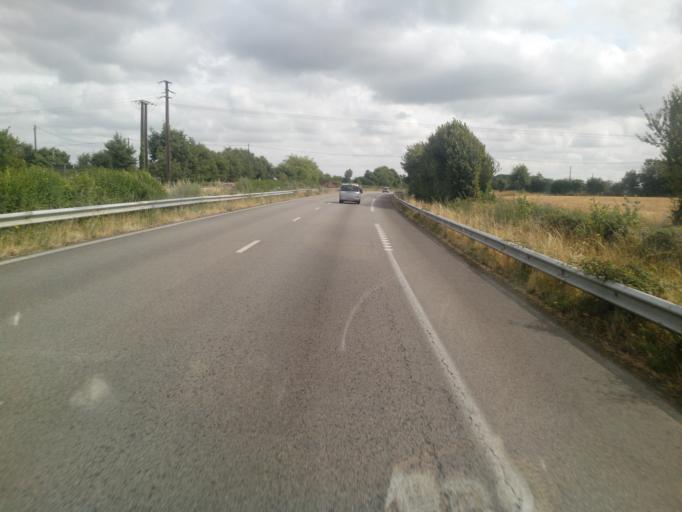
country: FR
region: Pays de la Loire
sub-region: Departement de la Loire-Atlantique
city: Nozay
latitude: 47.5551
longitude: -1.6328
